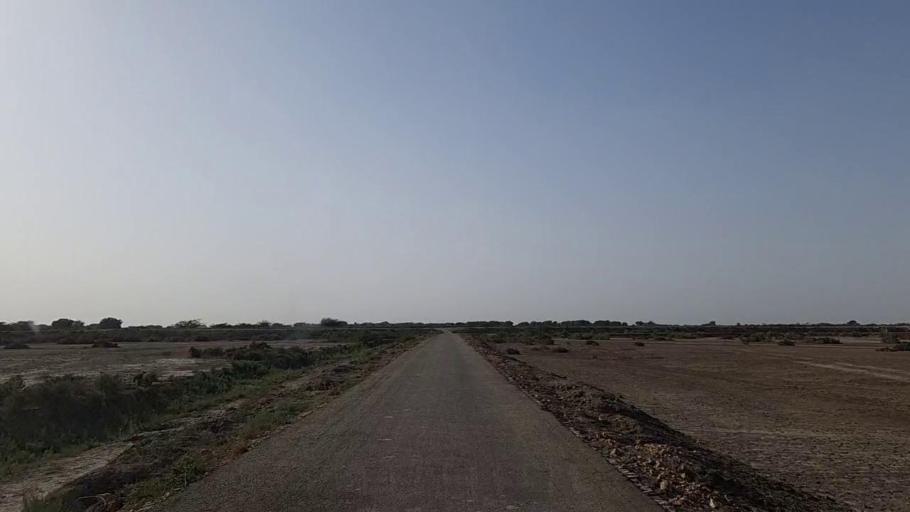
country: PK
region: Sindh
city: Jati
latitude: 24.3035
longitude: 68.1965
